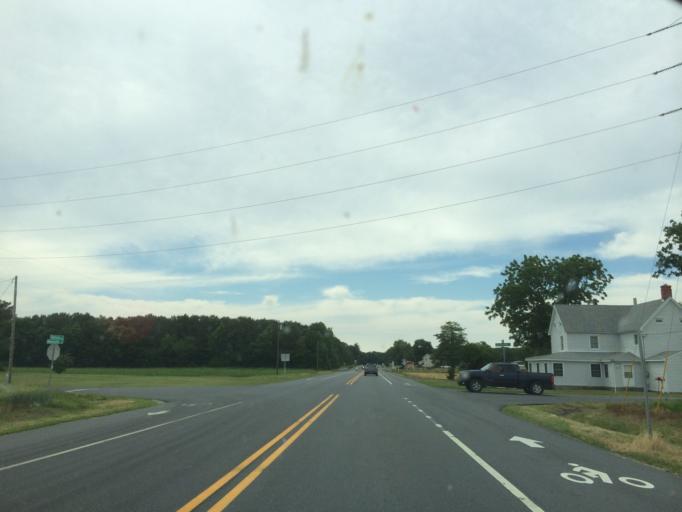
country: US
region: Delaware
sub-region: Sussex County
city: Bridgeville
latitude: 38.7970
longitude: -75.7011
